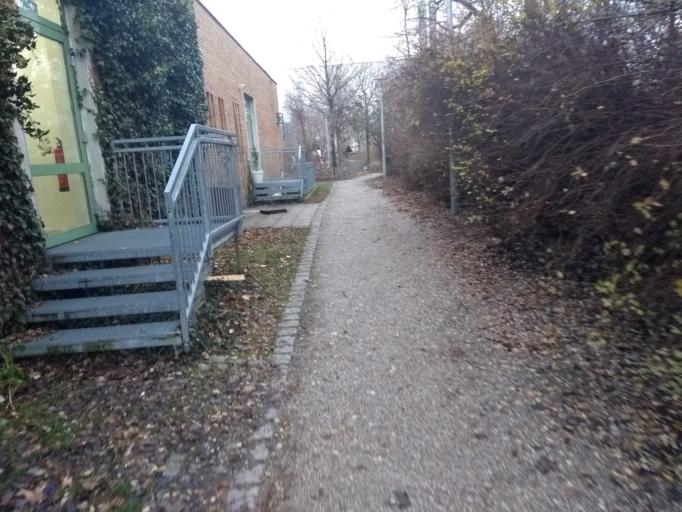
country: DE
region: Bavaria
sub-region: Upper Bavaria
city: Munich
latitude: 48.1386
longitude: 11.5412
